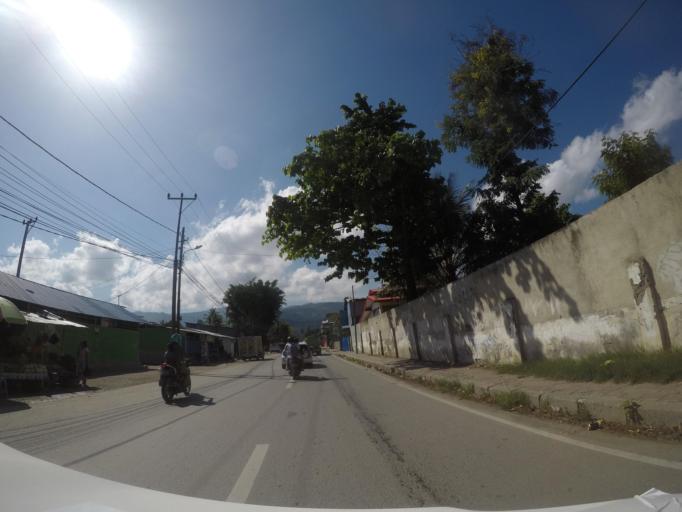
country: TL
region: Dili
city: Dili
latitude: -8.5520
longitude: 125.5904
